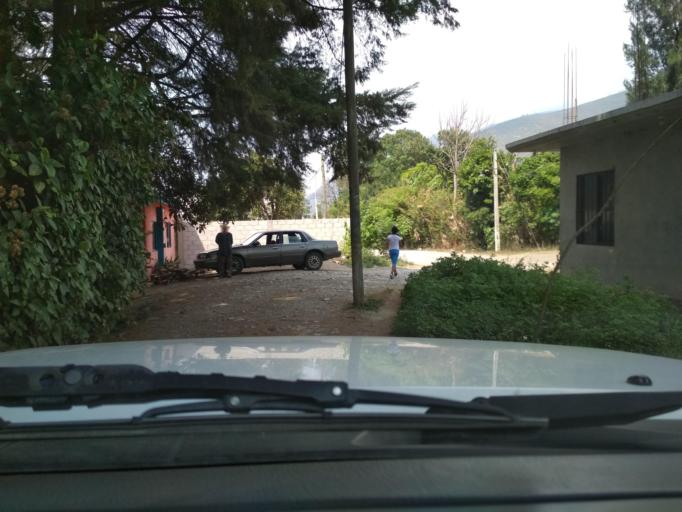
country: MX
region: Veracruz
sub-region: Acultzingo
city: Acatla
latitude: 18.7646
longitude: -97.2205
